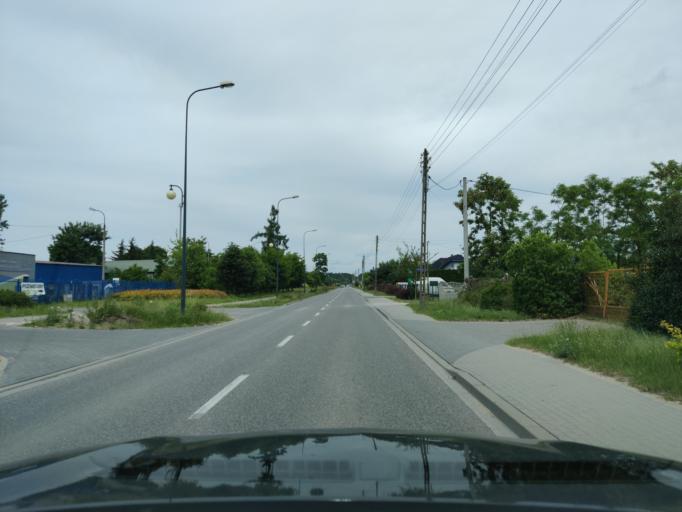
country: PL
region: Masovian Voivodeship
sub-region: Powiat wyszkowski
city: Wyszkow
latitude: 52.6121
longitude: 21.4537
